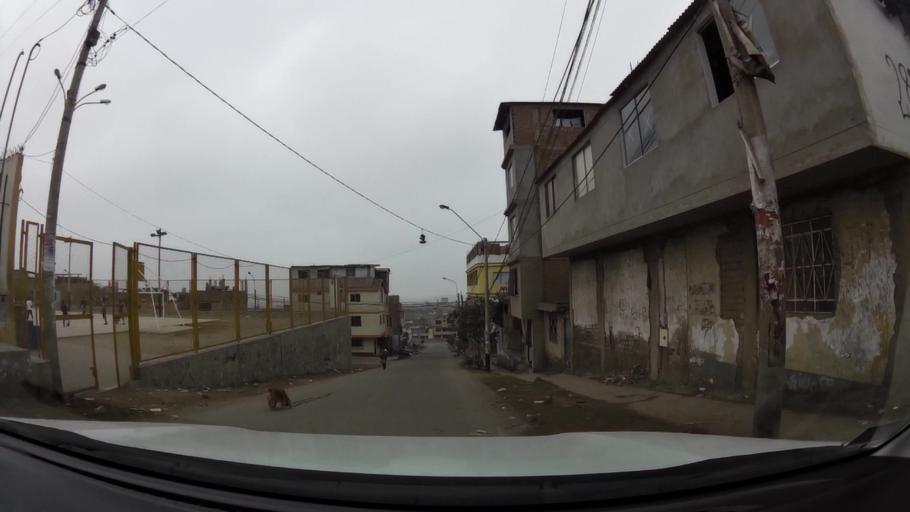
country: PE
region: Lima
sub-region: Lima
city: Surco
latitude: -12.1517
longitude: -76.9634
